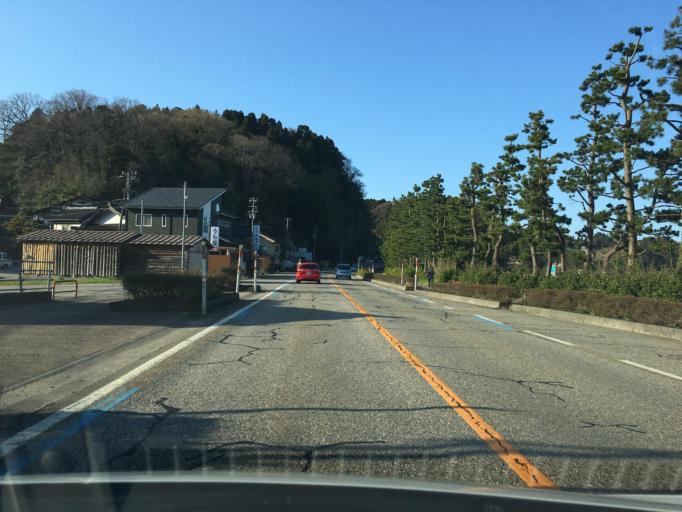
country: JP
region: Toyama
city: Himi
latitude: 36.9160
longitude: 137.0255
